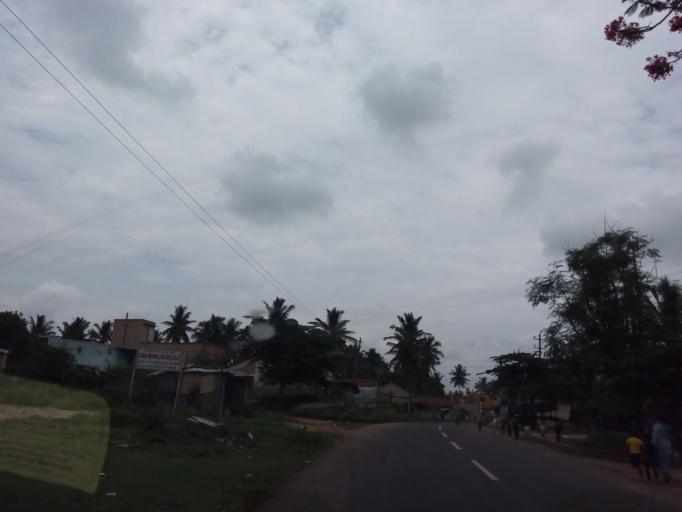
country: IN
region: Karnataka
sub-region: Hassan
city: Shravanabelagola
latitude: 12.8547
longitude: 76.4802
